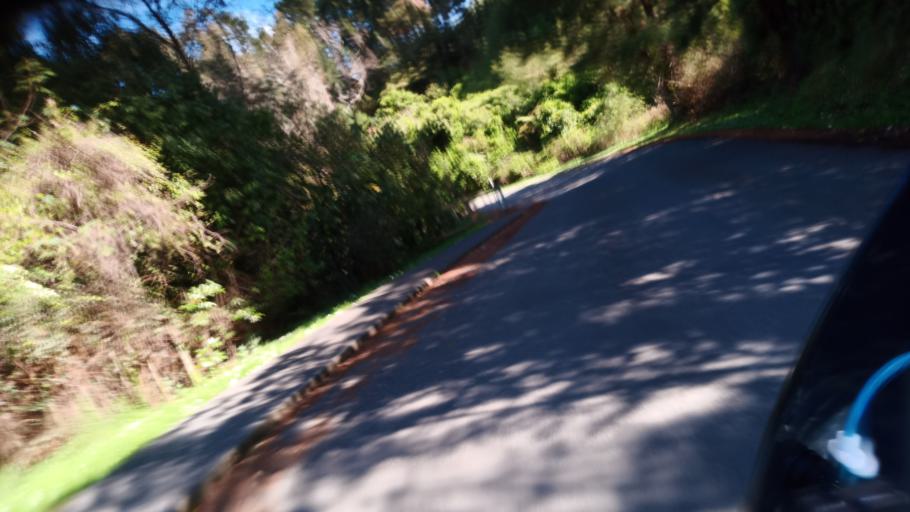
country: NZ
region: Hawke's Bay
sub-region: Wairoa District
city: Wairoa
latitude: -38.8171
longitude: 177.1448
